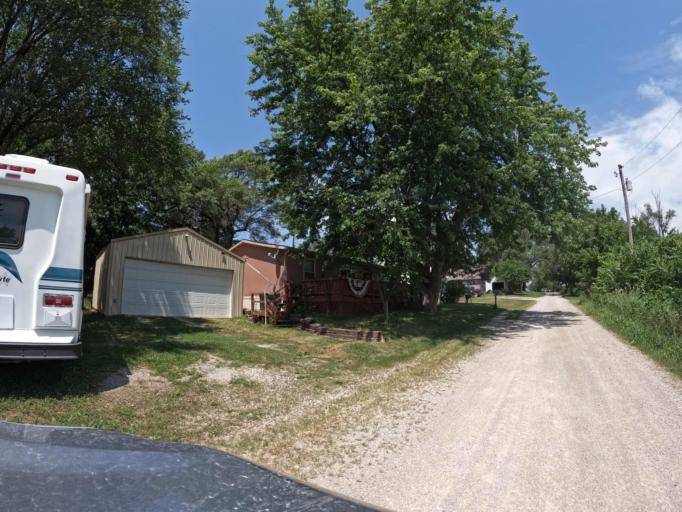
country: US
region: Iowa
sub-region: Appanoose County
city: Centerville
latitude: 40.7843
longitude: -92.9050
